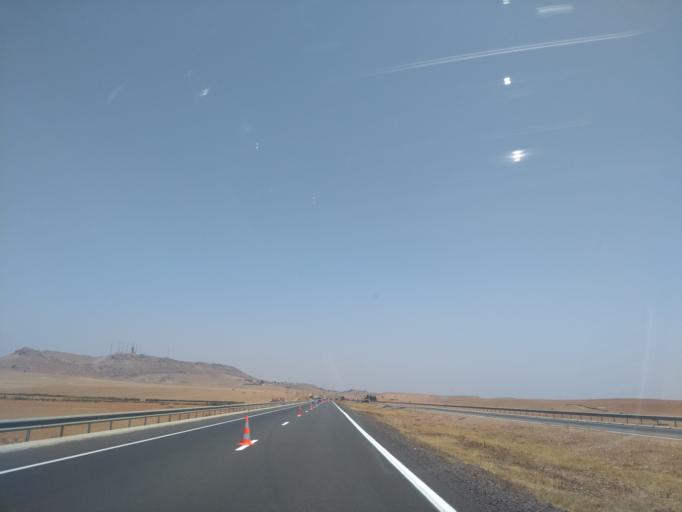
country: MA
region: Marrakech-Tensift-Al Haouz
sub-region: Kelaa-Des-Sraghna
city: Sidi Abdallah
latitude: 32.4520
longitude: -7.9314
